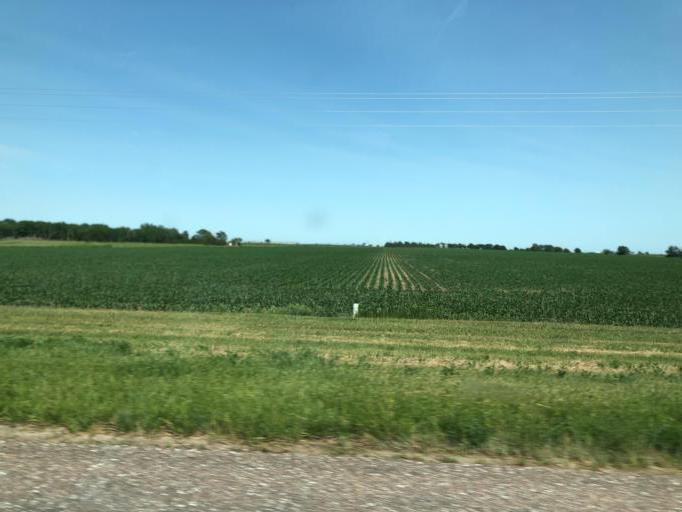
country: US
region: Nebraska
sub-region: Fillmore County
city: Geneva
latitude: 40.4902
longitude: -97.5959
